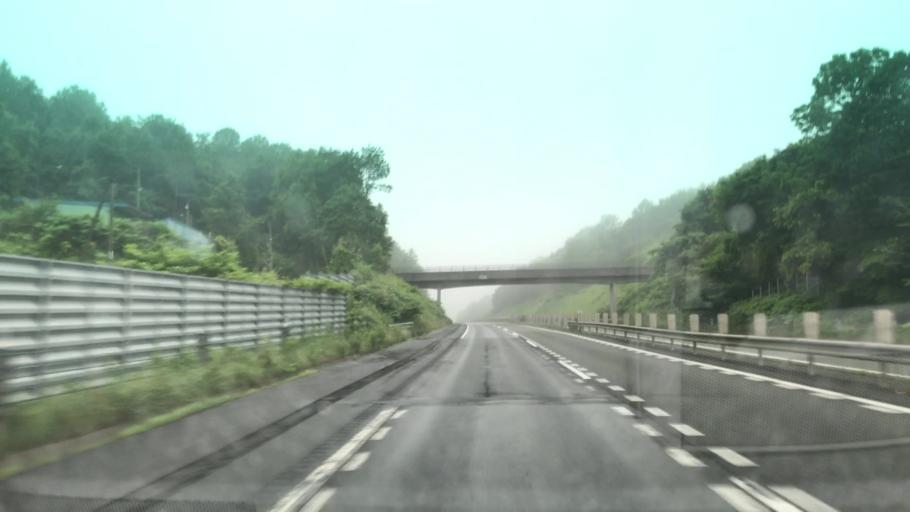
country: JP
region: Hokkaido
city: Tomakomai
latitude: 42.6482
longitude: 141.5369
